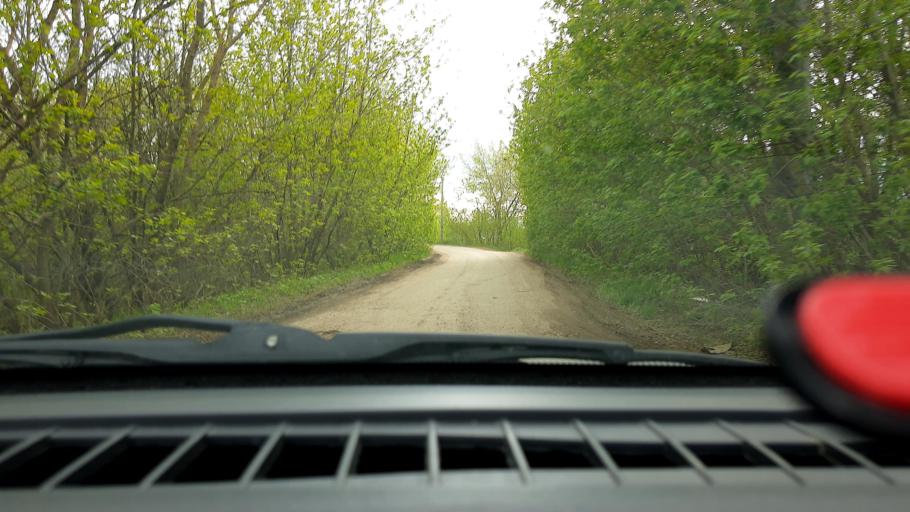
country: RU
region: Nizjnij Novgorod
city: Neklyudovo
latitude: 56.3850
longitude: 43.8381
